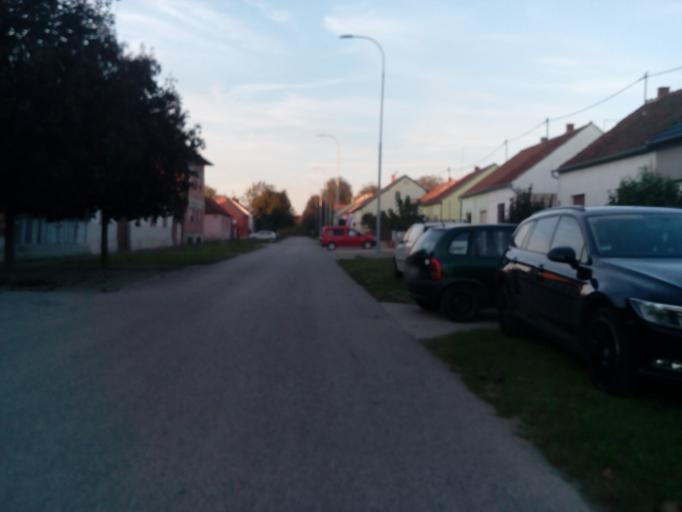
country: HR
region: Vukovarsko-Srijemska
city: Vinkovci
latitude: 45.2977
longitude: 18.8172
